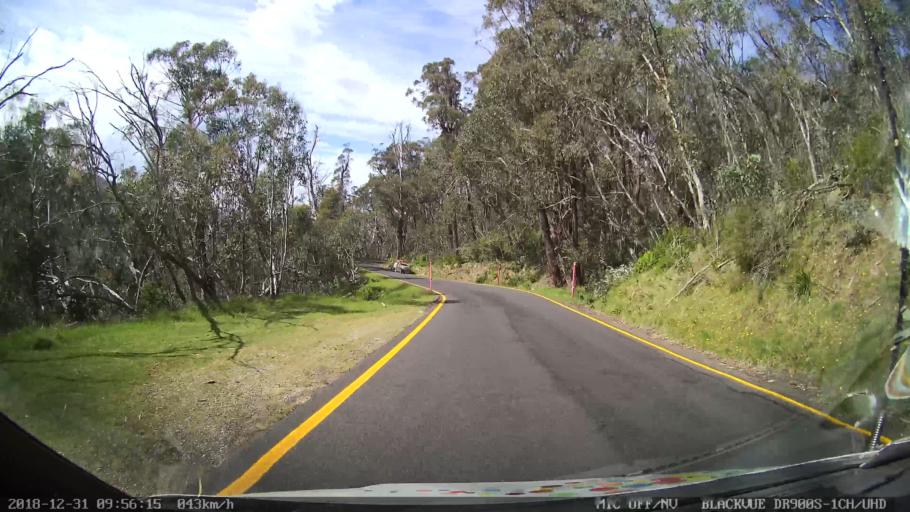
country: AU
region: New South Wales
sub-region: Snowy River
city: Jindabyne
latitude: -36.5302
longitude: 148.2252
